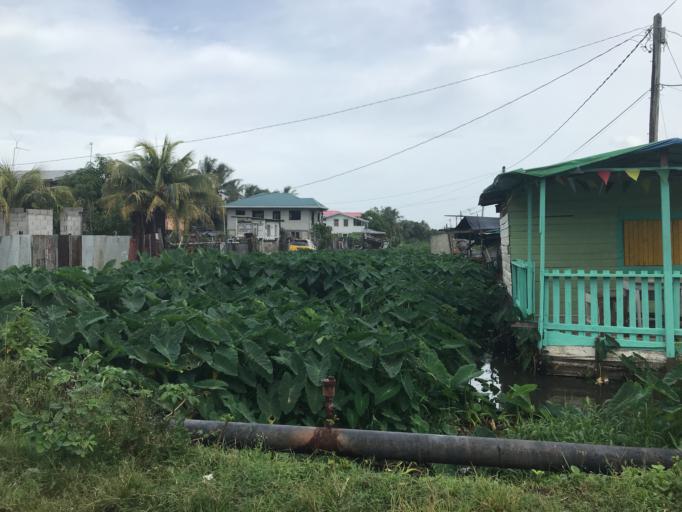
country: GY
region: Demerara-Mahaica
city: Georgetown
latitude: 6.8071
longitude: -58.1188
